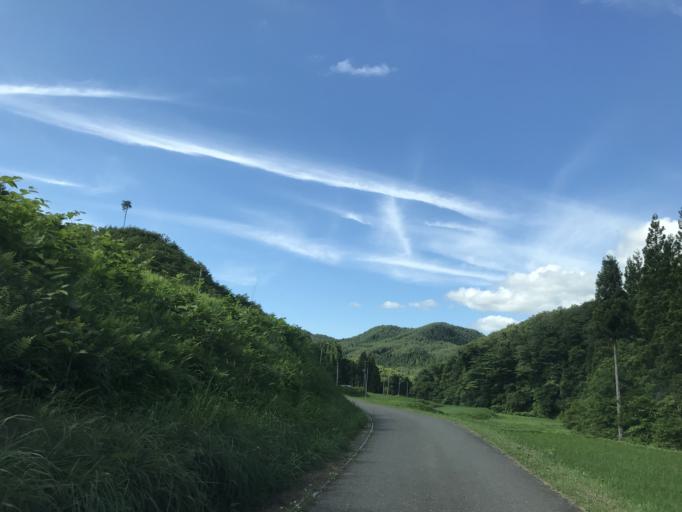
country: JP
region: Iwate
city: Ichinoseki
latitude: 38.9214
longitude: 140.9412
